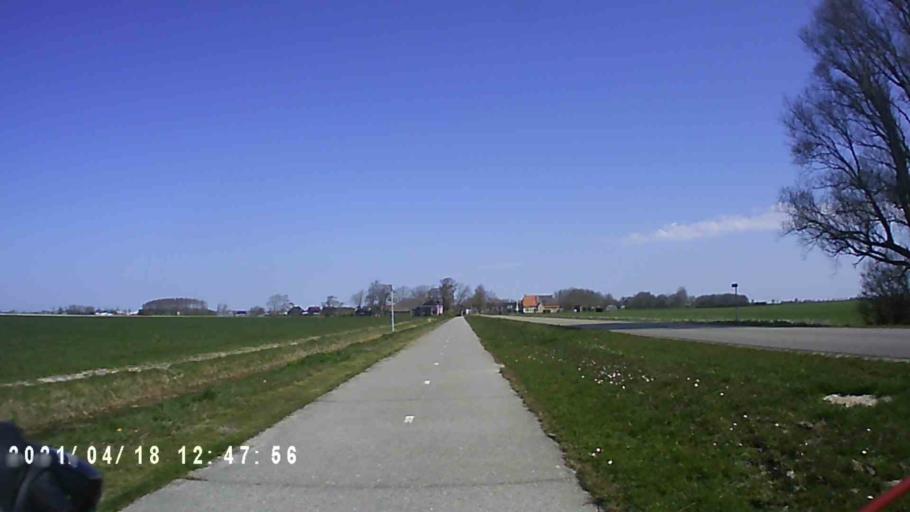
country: NL
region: Friesland
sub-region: Gemeente Dongeradeel
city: Dokkum
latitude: 53.3717
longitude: 6.0504
